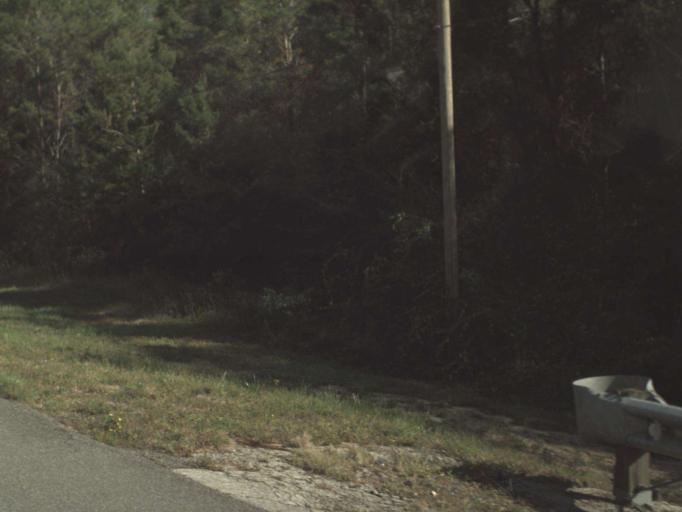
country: US
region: Florida
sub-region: Bay County
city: Youngstown
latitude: 30.4353
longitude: -85.4015
